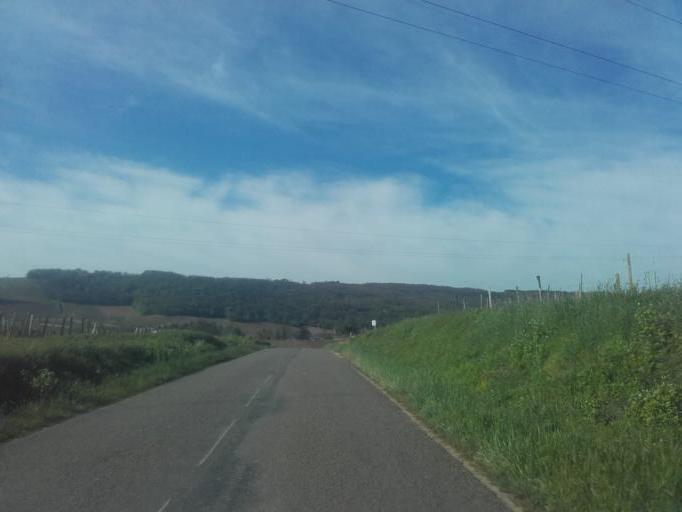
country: FR
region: Bourgogne
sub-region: Departement de Saone-et-Loire
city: Prisse
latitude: 46.2867
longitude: 4.7508
